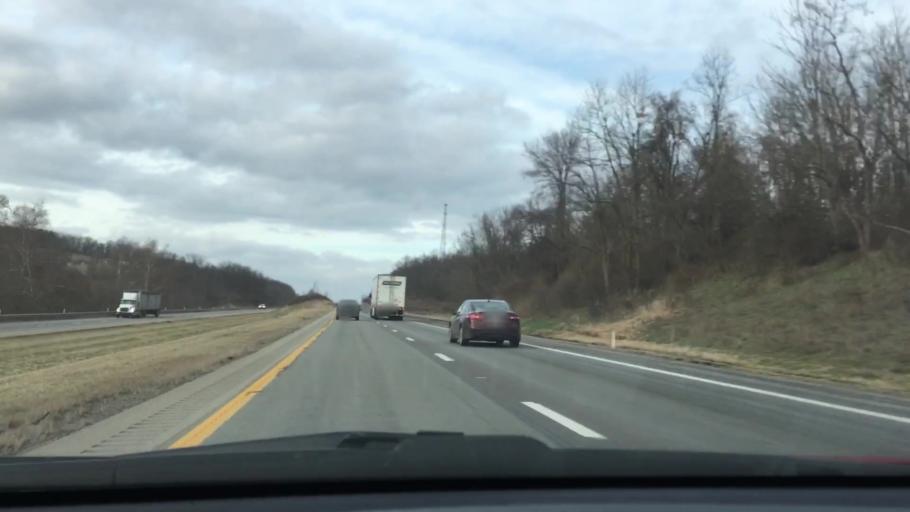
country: US
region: Pennsylvania
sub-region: Washington County
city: East Washington
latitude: 40.0668
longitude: -80.1877
